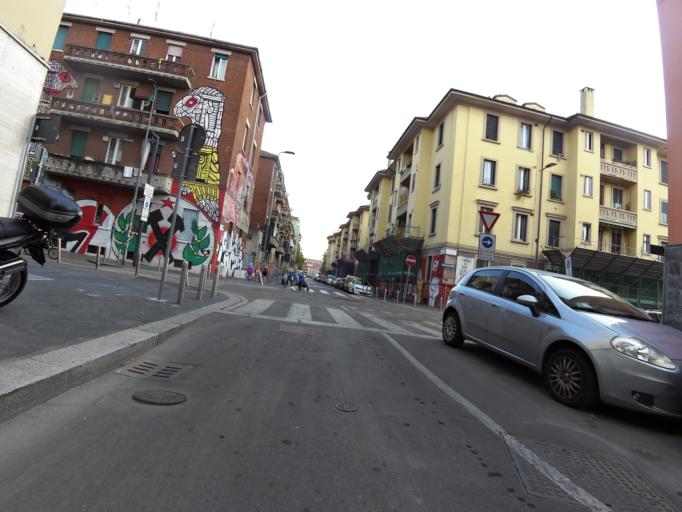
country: IT
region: Lombardy
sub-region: Citta metropolitana di Milano
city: Milano
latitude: 45.4492
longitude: 9.1754
